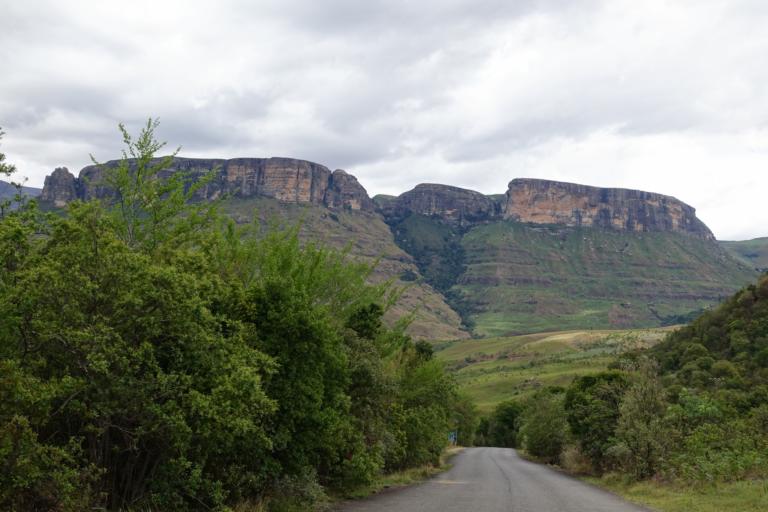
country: ZA
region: Orange Free State
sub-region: Thabo Mofutsanyana District Municipality
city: Phuthaditjhaba
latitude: -28.6845
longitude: 28.9589
